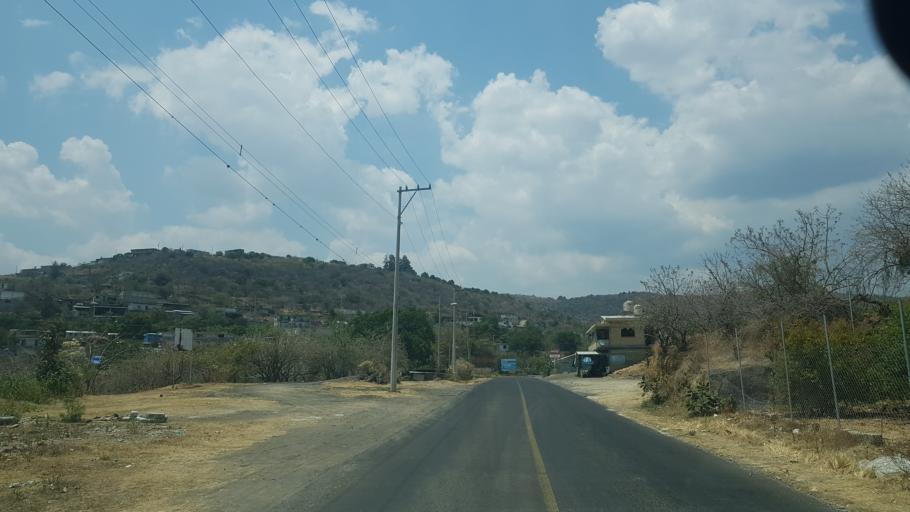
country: MX
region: Puebla
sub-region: Atzitzihuacan
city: Santiago Atzitzihuacan
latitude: 18.8350
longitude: -98.5945
